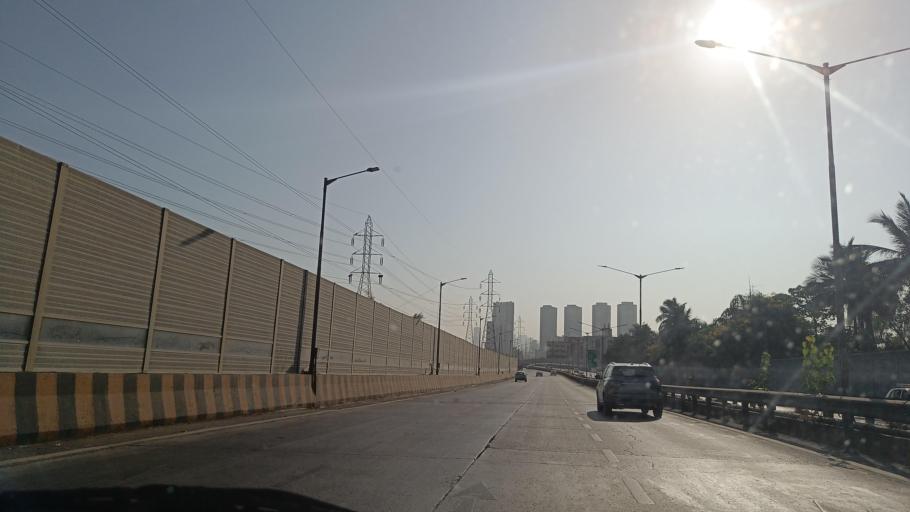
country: IN
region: Maharashtra
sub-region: Mumbai Suburban
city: Mumbai
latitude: 19.0314
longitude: 72.8927
